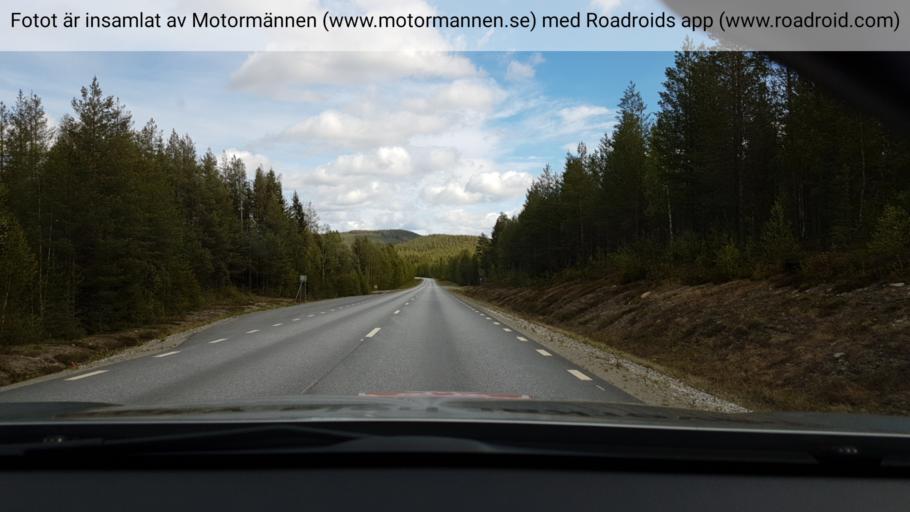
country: SE
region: Vaesterbotten
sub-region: Asele Kommun
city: Insjon
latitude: 64.1983
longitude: 17.6638
